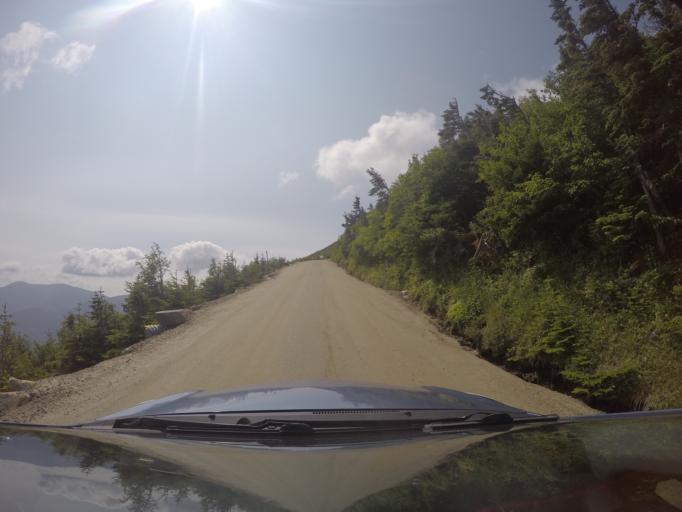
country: US
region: New Hampshire
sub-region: Coos County
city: Gorham
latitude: 44.2884
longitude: -71.2797
